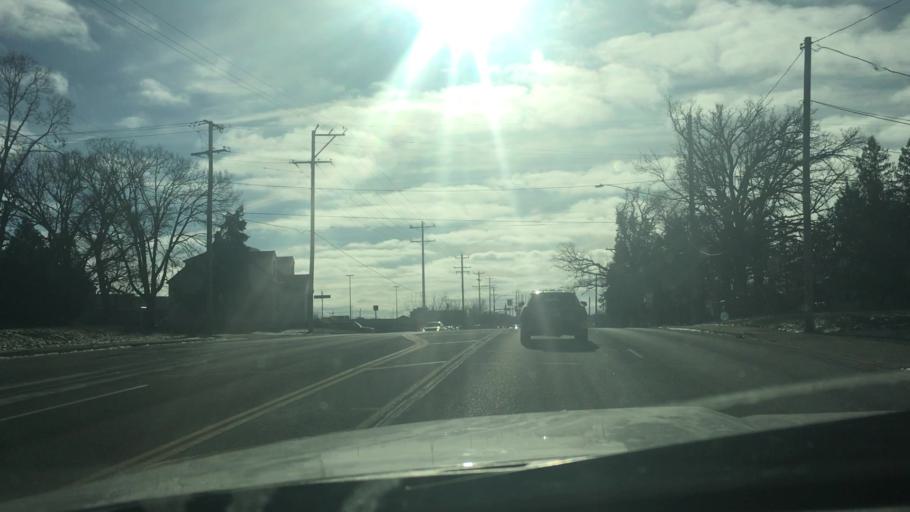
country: US
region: Minnesota
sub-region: Stearns County
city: Waite Park
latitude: 45.5584
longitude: -94.2138
